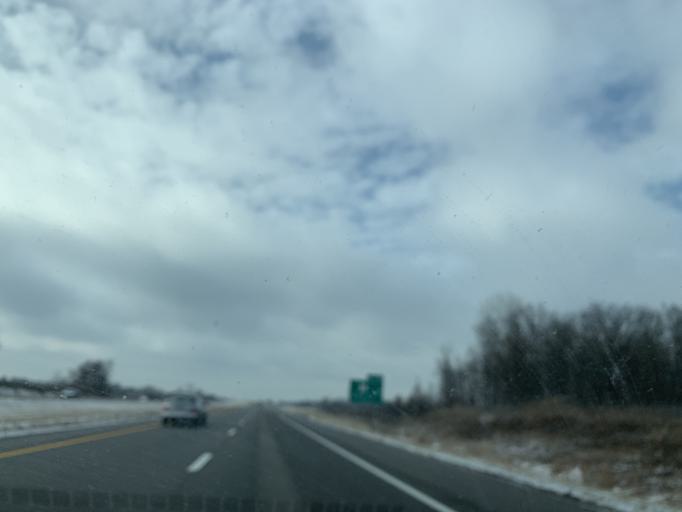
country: US
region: Ohio
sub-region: Licking County
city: Johnstown
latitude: 40.0807
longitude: -82.7137
